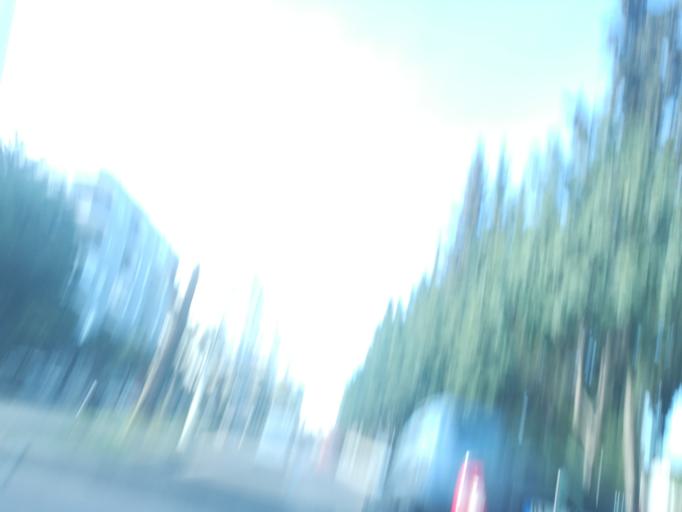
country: TR
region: Adana
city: Adana
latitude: 37.0316
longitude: 35.3228
